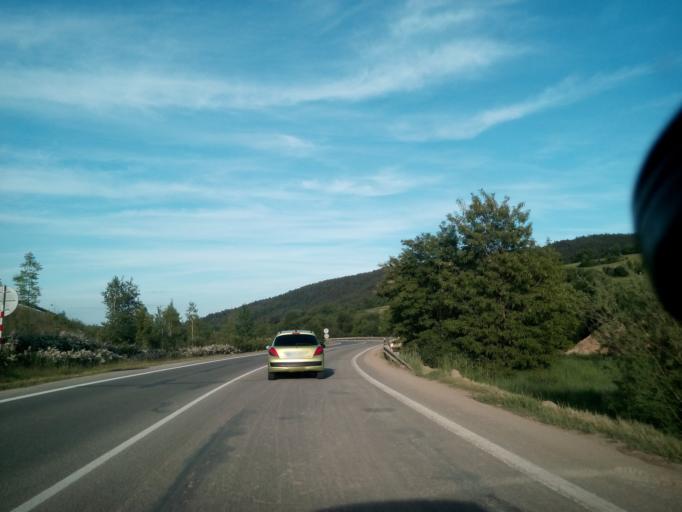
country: SK
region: Presovsky
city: Lipany
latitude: 49.0202
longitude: 20.9845
